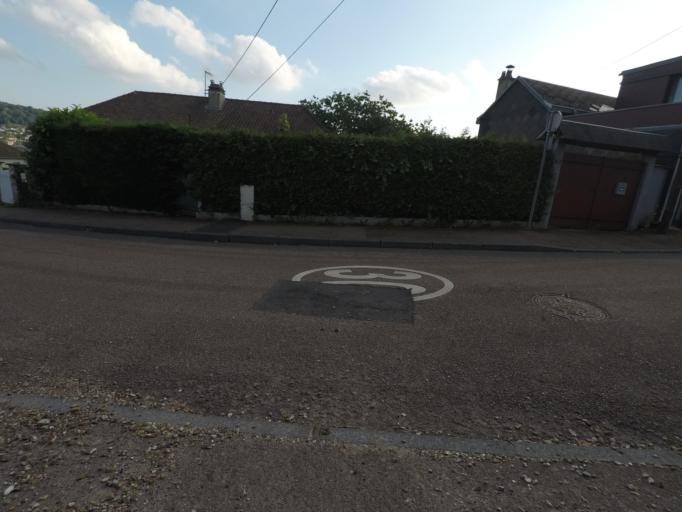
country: FR
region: Haute-Normandie
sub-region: Departement de la Seine-Maritime
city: Bihorel
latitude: 49.4444
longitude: 1.1196
